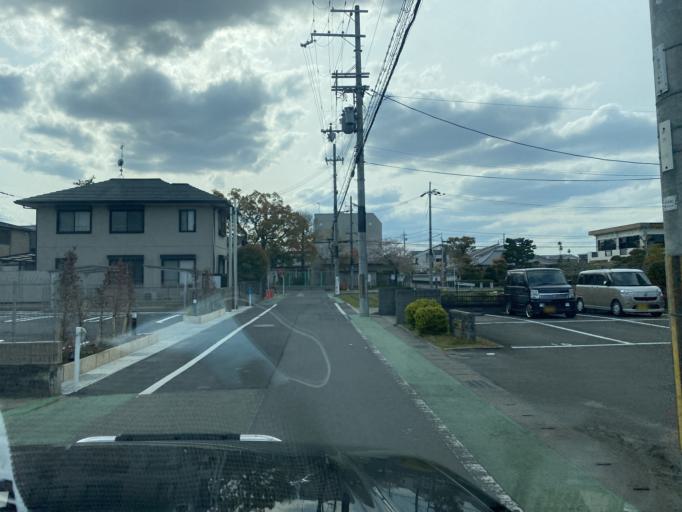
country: JP
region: Kyoto
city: Tanabe
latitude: 34.8119
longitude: 135.7867
